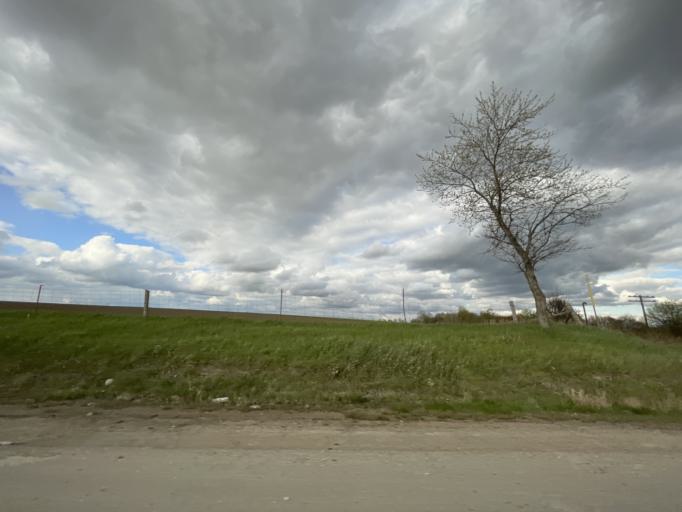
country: CA
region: Ontario
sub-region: Wellington County
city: Guelph
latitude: 43.5154
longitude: -80.3188
